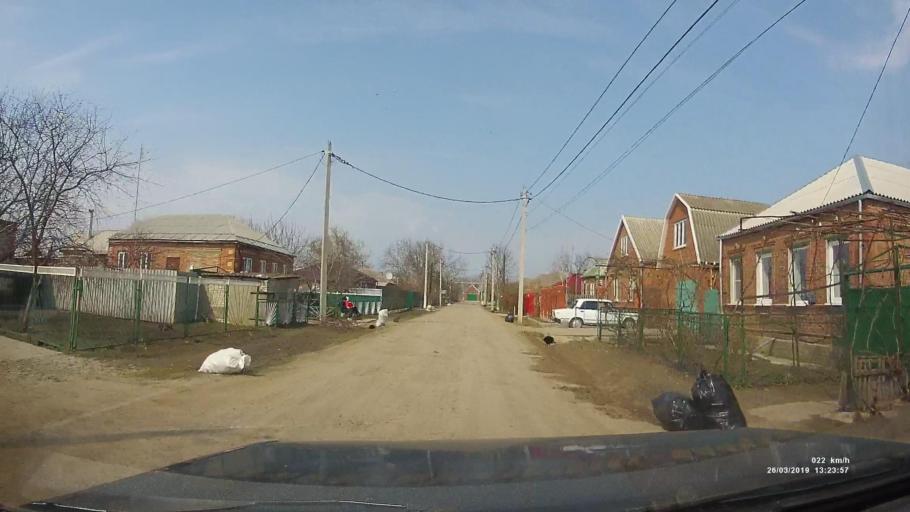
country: RU
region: Rostov
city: Novobessergenovka
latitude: 47.1736
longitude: 38.7662
